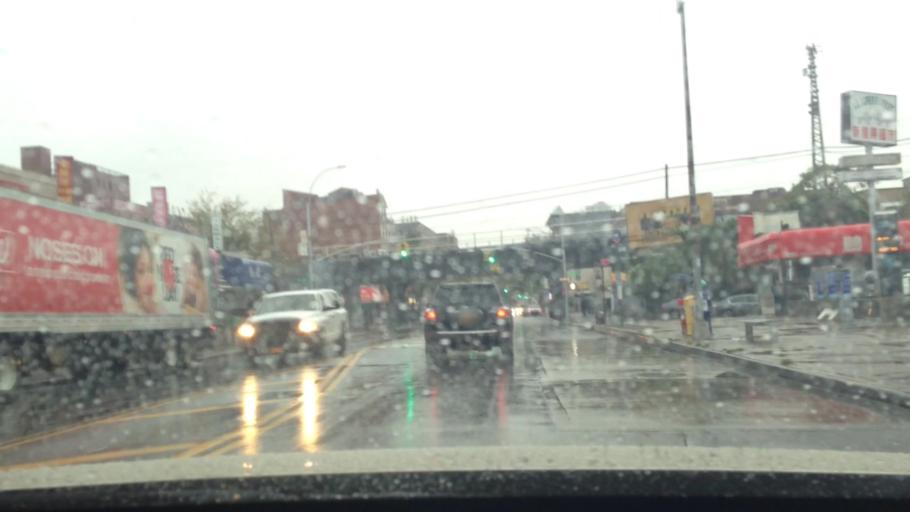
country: US
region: New York
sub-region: Queens County
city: Long Island City
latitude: 40.7418
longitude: -73.8808
